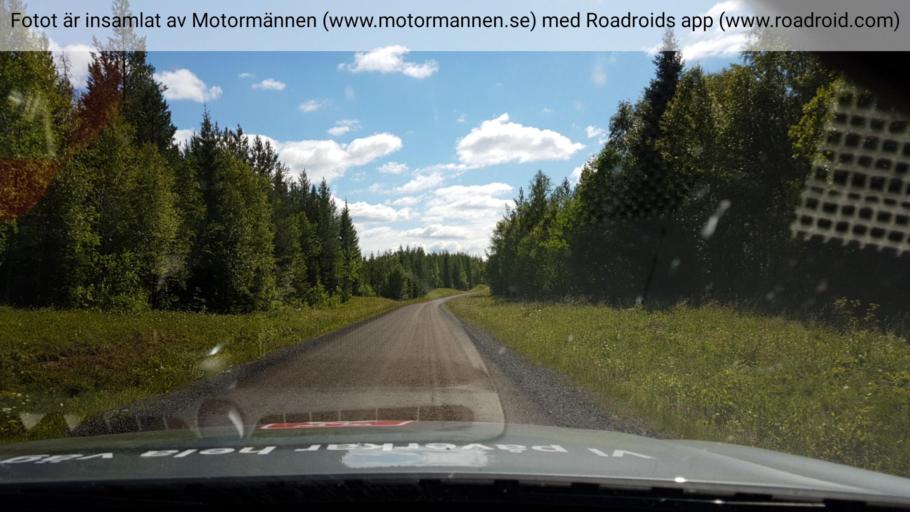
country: SE
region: Jaemtland
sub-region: OEstersunds Kommun
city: Lit
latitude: 63.4014
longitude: 15.2313
